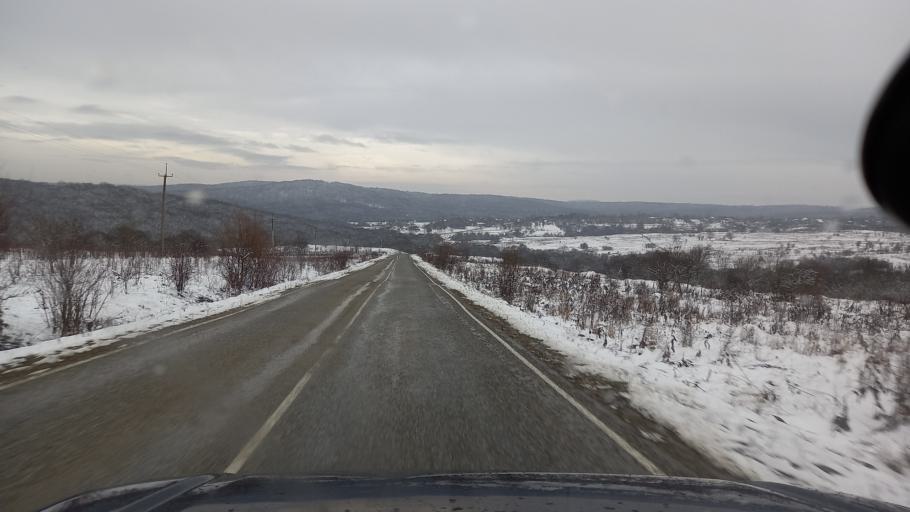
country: RU
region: Adygeya
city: Abadzekhskaya
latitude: 44.3591
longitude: 40.3891
